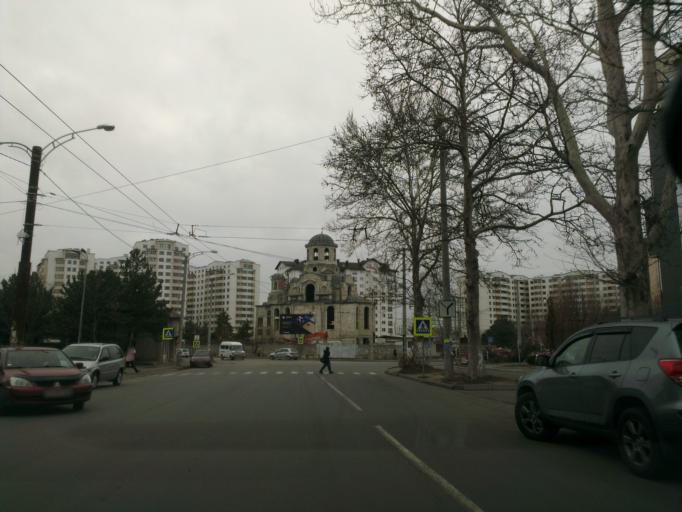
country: MD
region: Chisinau
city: Chisinau
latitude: 46.9857
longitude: 28.8451
